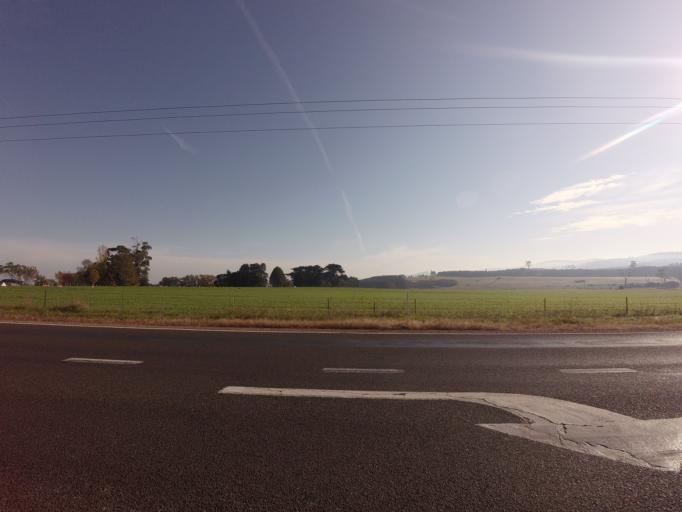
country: AU
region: Tasmania
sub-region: Launceston
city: Summerhill
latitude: -41.5254
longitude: 147.0286
